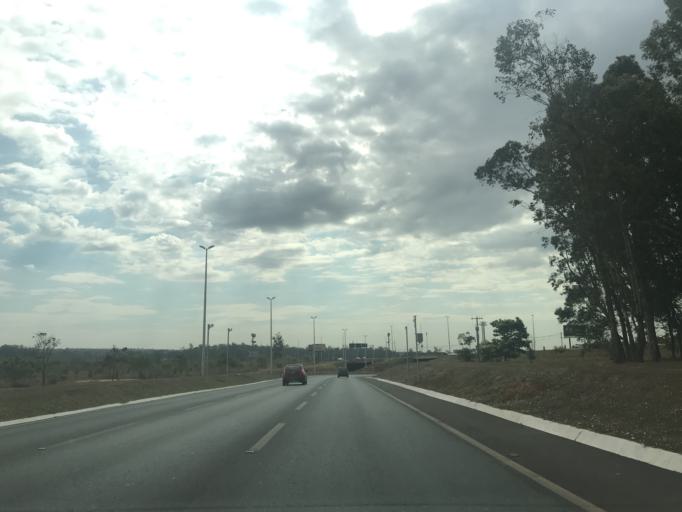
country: BR
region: Federal District
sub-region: Brasilia
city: Brasilia
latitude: -15.8598
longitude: -47.9361
